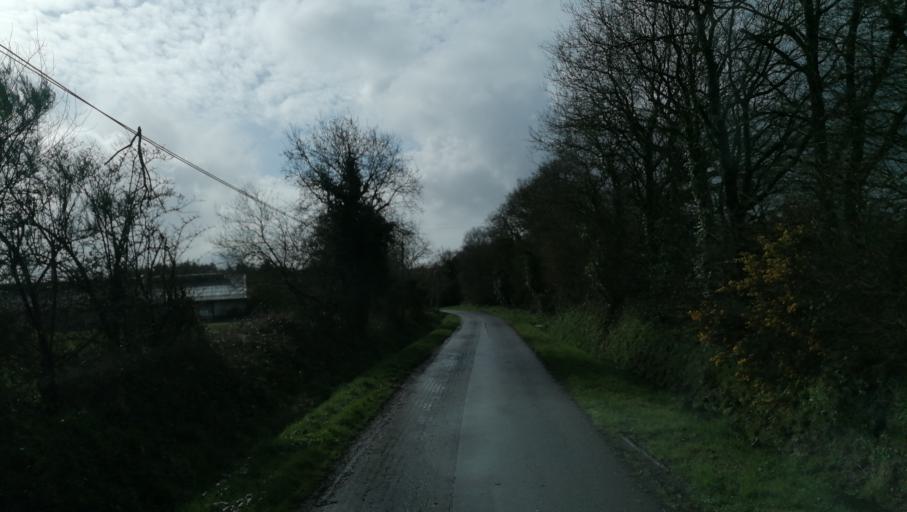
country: FR
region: Brittany
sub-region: Departement des Cotes-d'Armor
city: Lanrodec
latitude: 48.4999
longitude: -3.0267
